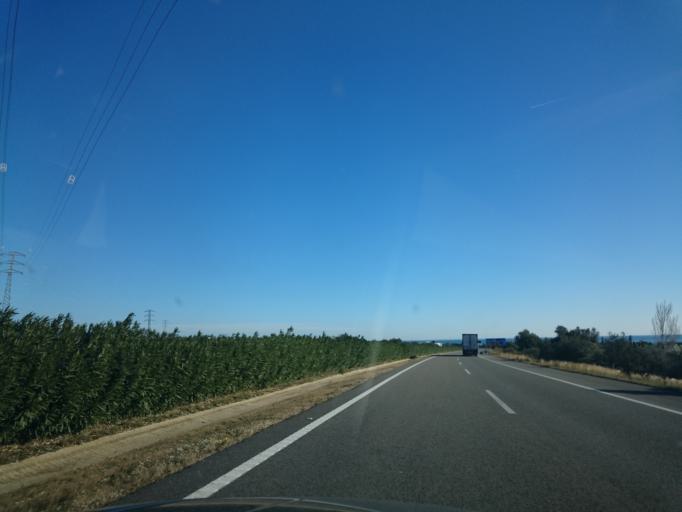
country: ES
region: Catalonia
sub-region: Provincia de Tarragona
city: L'Ampolla
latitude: 40.8025
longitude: 0.6804
